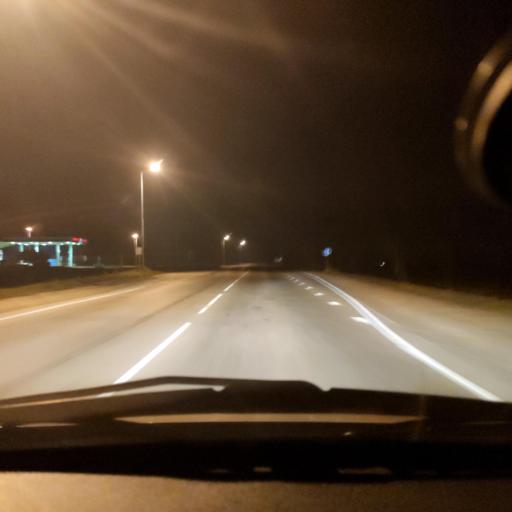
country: RU
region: Bashkortostan
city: Iglino
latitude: 54.8663
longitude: 56.4610
